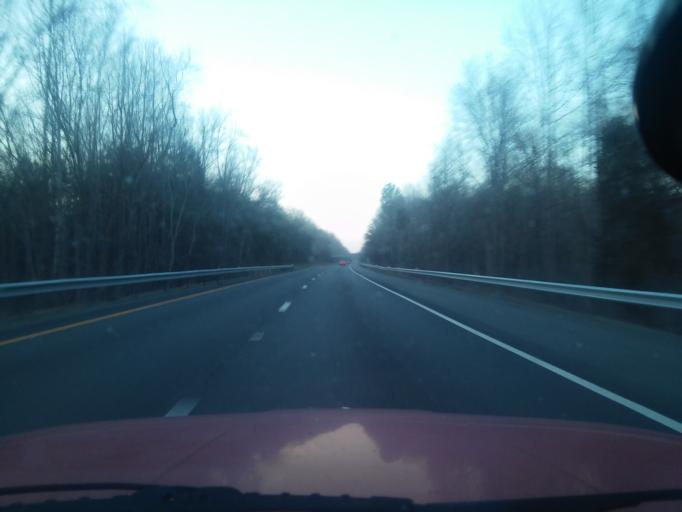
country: US
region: Virginia
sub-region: Goochland County
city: Goochland
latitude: 37.7266
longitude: -77.8204
